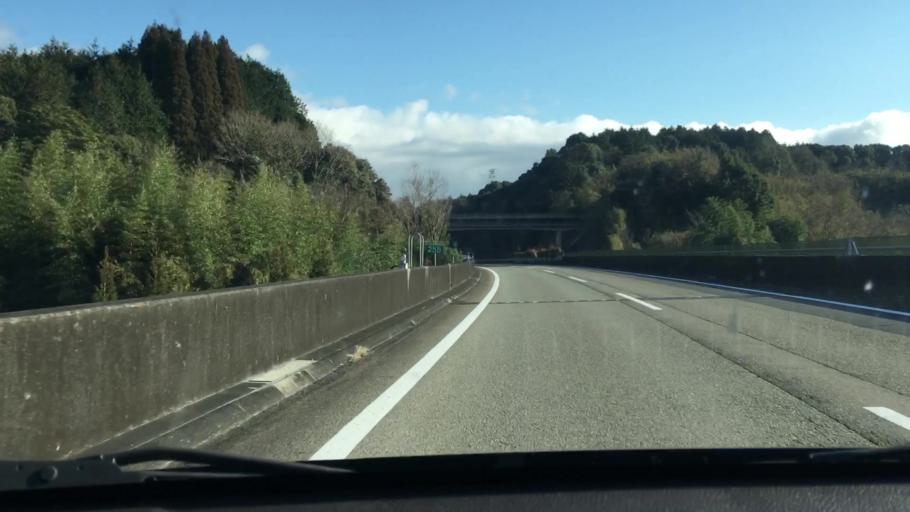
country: JP
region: Kumamoto
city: Hitoyoshi
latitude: 32.1853
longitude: 130.7780
